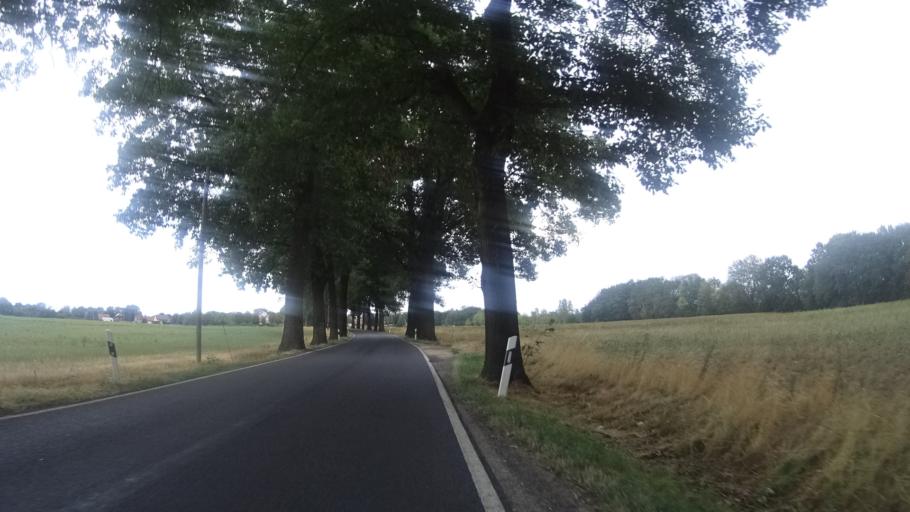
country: DE
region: Saxony
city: Rothenburg
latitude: 51.3062
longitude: 15.0041
